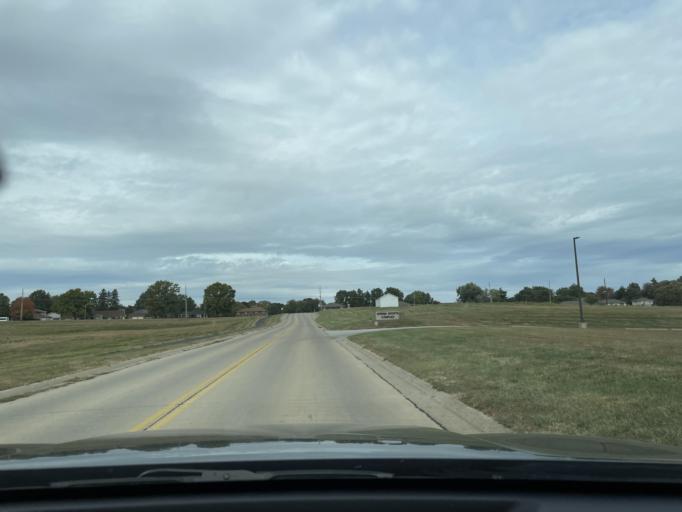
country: US
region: Missouri
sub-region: Buchanan County
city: Saint Joseph
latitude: 39.7673
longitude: -94.7811
